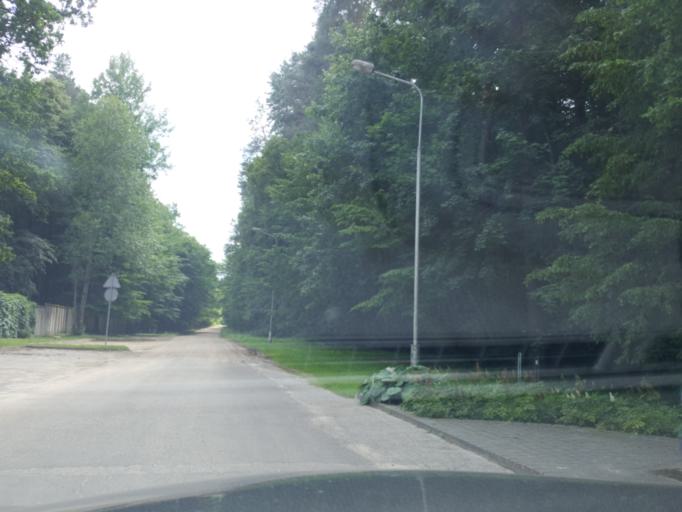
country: LT
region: Alytaus apskritis
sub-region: Alytus
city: Alytus
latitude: 54.3817
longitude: 24.0420
